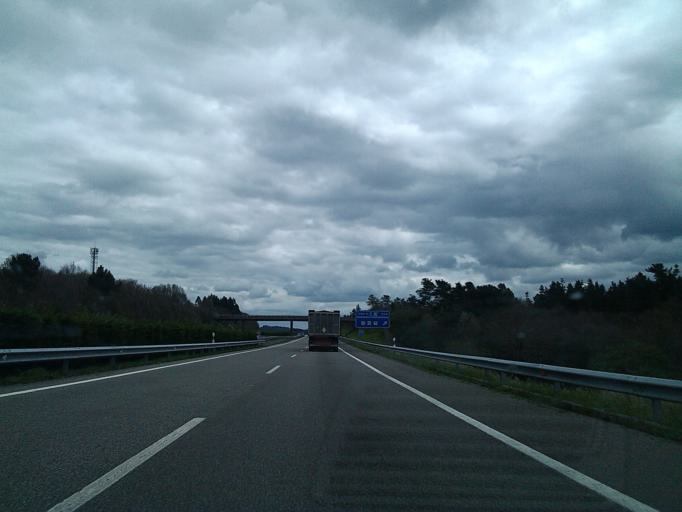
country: ES
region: Galicia
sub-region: Provincia de Lugo
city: Guitiriz
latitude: 43.1875
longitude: -7.8466
